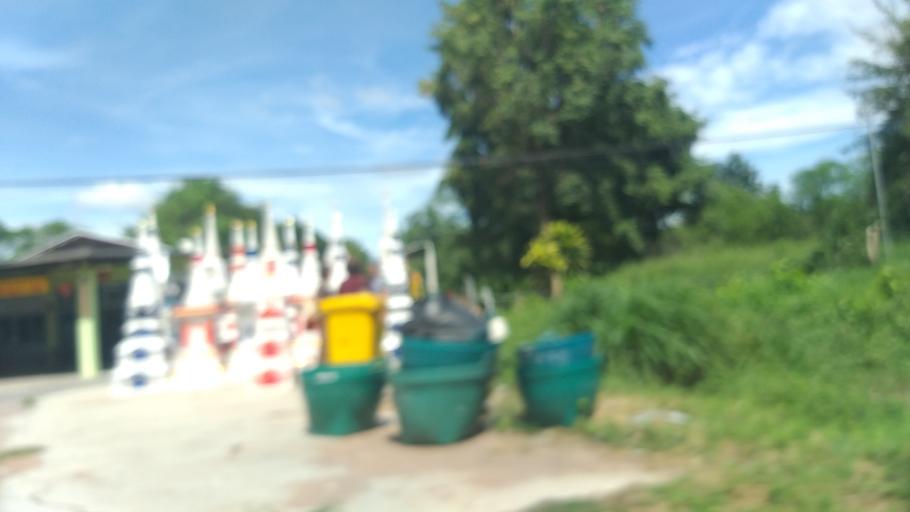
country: TH
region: Khon Kaen
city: Nong Ruea
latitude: 16.4868
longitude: 102.4350
